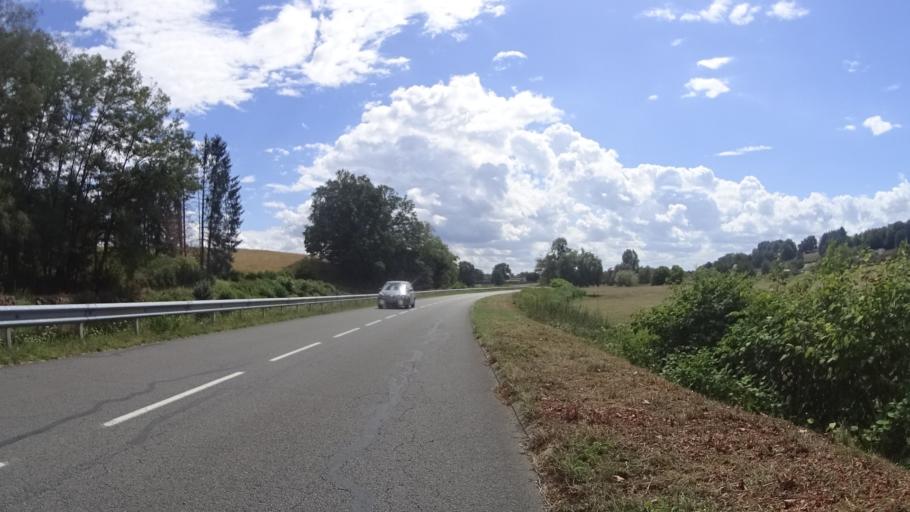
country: FR
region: Bourgogne
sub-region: Departement de Saone-et-Loire
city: Saint-Vallier
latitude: 46.6367
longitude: 4.3348
